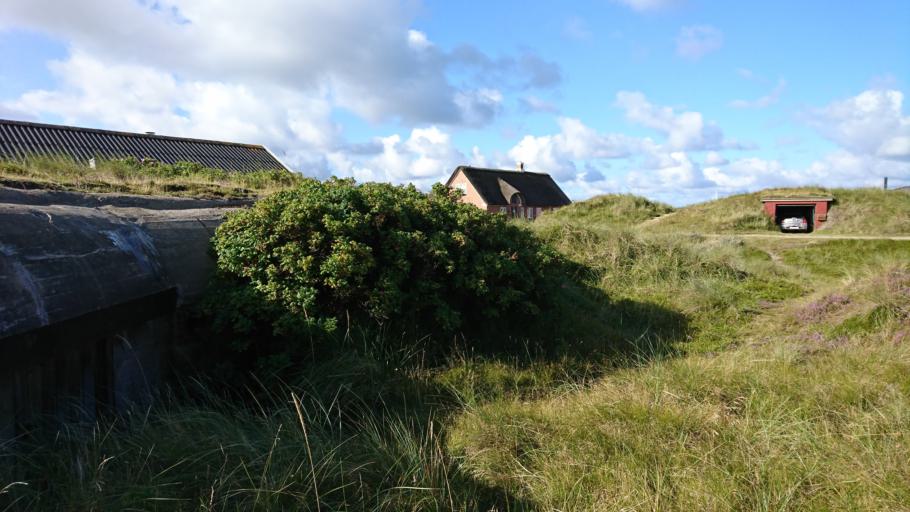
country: DK
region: South Denmark
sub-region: Fano Kommune
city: Nordby
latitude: 55.4275
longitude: 8.3745
